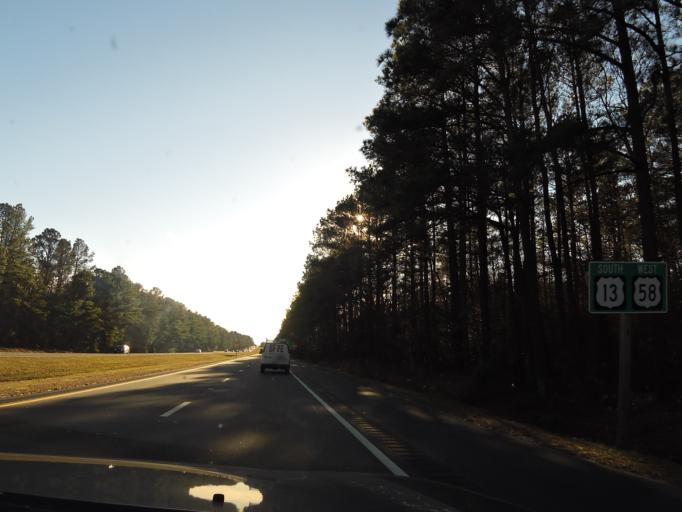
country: US
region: Virginia
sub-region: City of Suffolk
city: Suffolk
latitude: 36.7400
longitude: -76.6195
